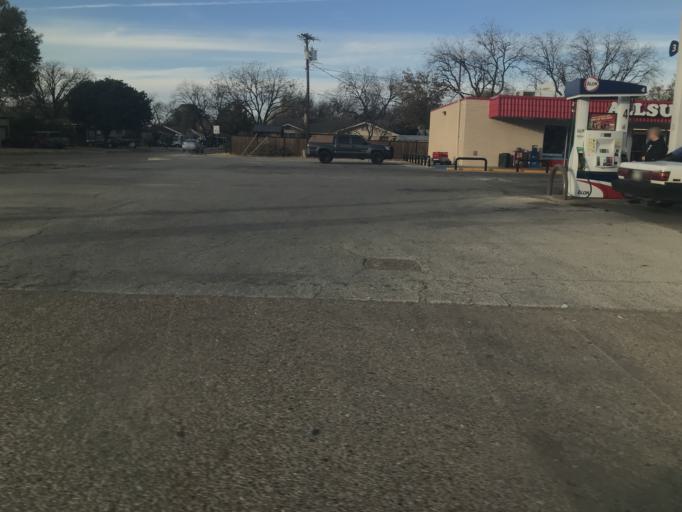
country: US
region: Texas
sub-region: Taylor County
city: Abilene
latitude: 32.4323
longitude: -99.7510
